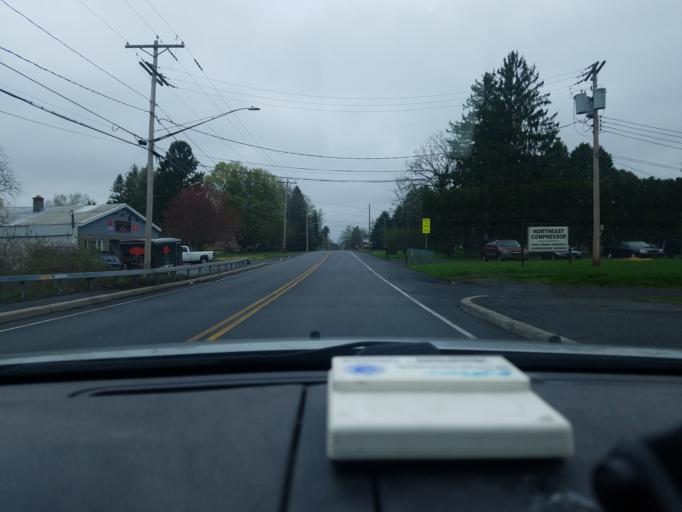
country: US
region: New York
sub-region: Onondaga County
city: North Syracuse
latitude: 43.1253
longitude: -76.0999
